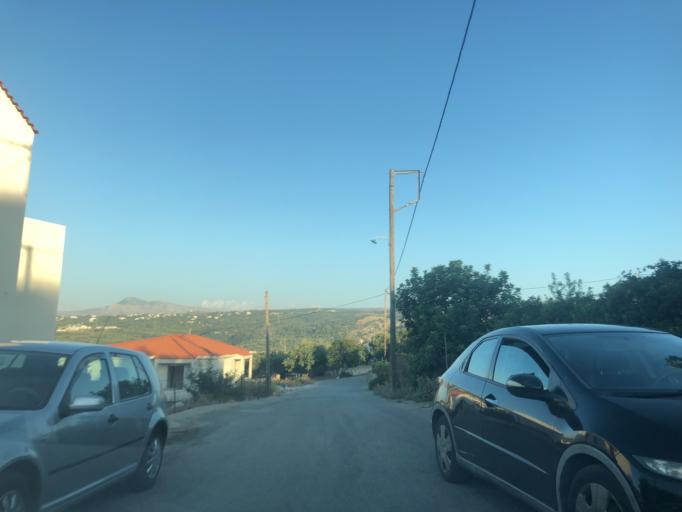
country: GR
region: Crete
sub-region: Nomos Rethymnis
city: Atsipopoulon
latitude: 35.3548
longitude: 24.3975
